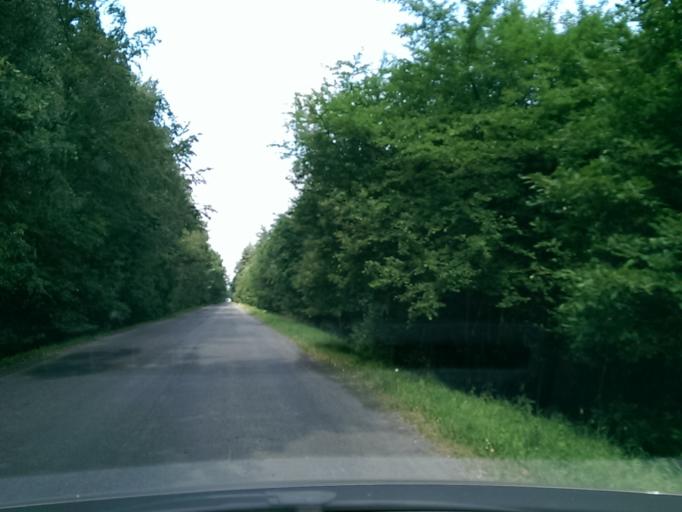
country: CZ
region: Central Bohemia
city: Kosmonosy
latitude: 50.4754
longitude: 14.8746
